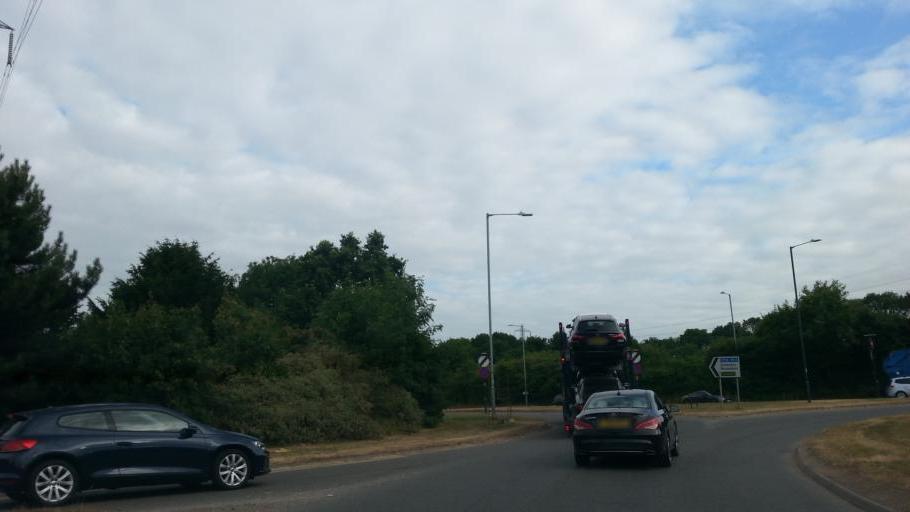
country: GB
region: England
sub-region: Warwickshire
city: Exhall
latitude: 52.4580
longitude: -1.4860
